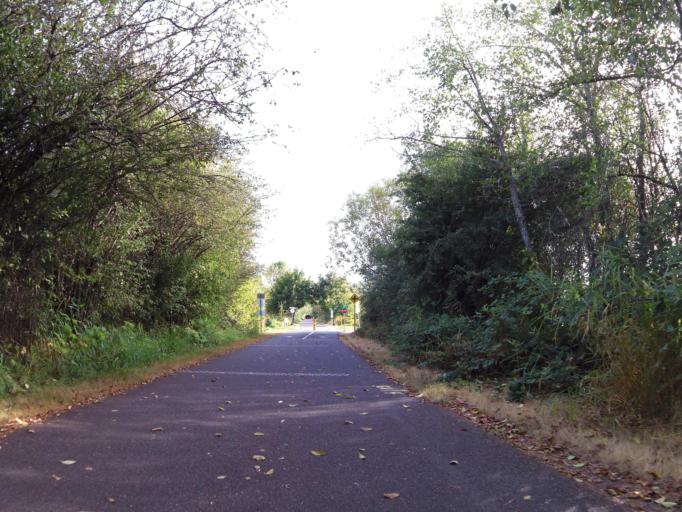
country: US
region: Washington
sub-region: Thurston County
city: Lacey
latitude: 47.0148
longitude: -122.8339
